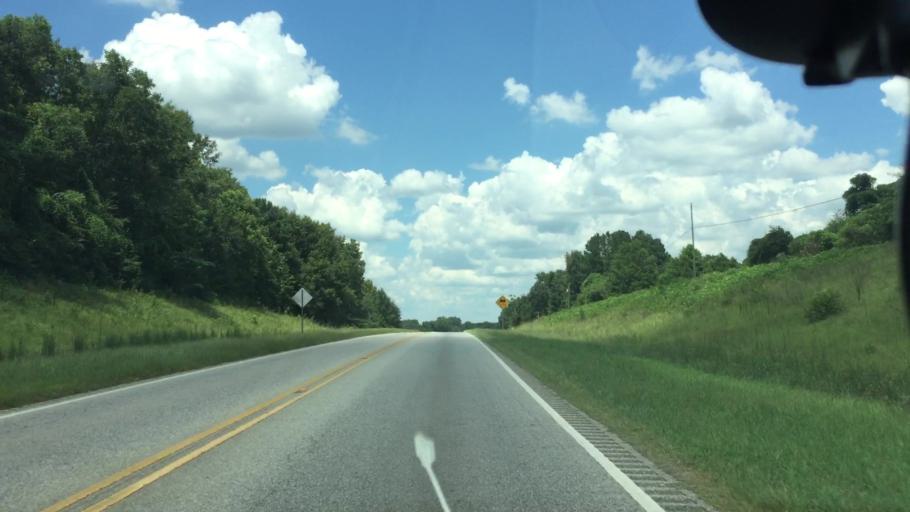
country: US
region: Alabama
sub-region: Pike County
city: Troy
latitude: 31.7120
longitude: -85.9590
